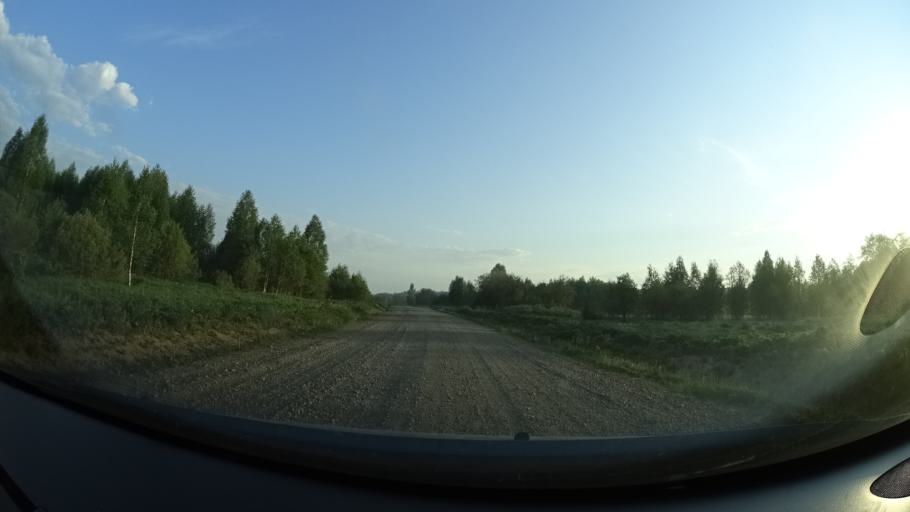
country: RU
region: Perm
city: Kuyeda
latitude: 56.6351
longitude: 55.7099
